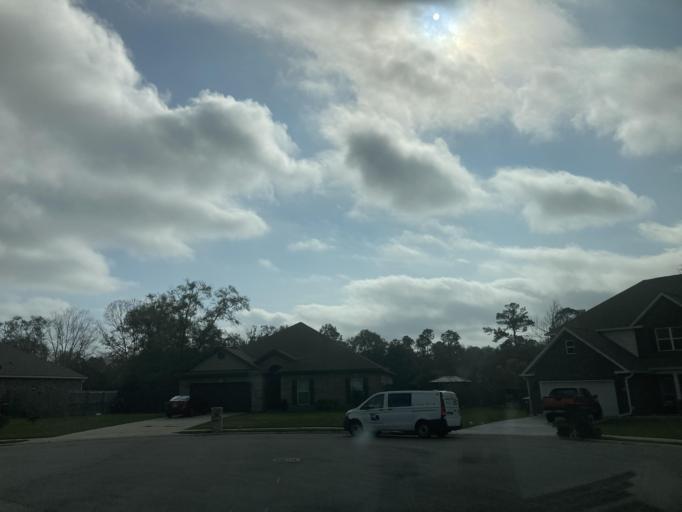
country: US
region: Mississippi
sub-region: Harrison County
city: D'Iberville
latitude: 30.4763
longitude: -88.9835
